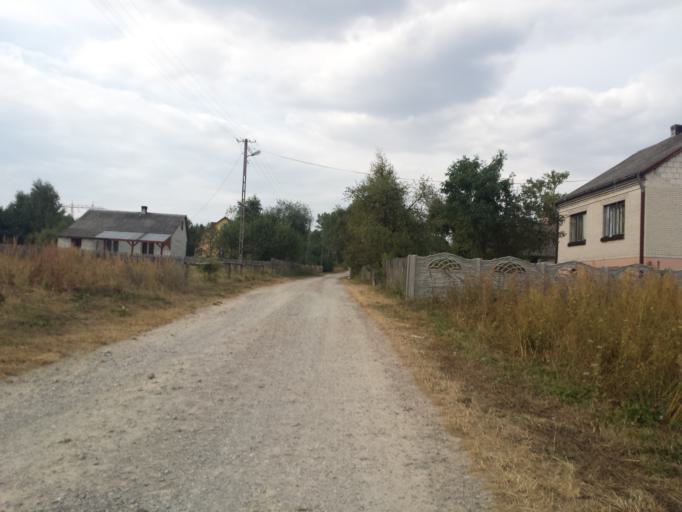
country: PL
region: Swietokrzyskie
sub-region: Powiat kielecki
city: Rakow
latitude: 50.6800
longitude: 21.0704
